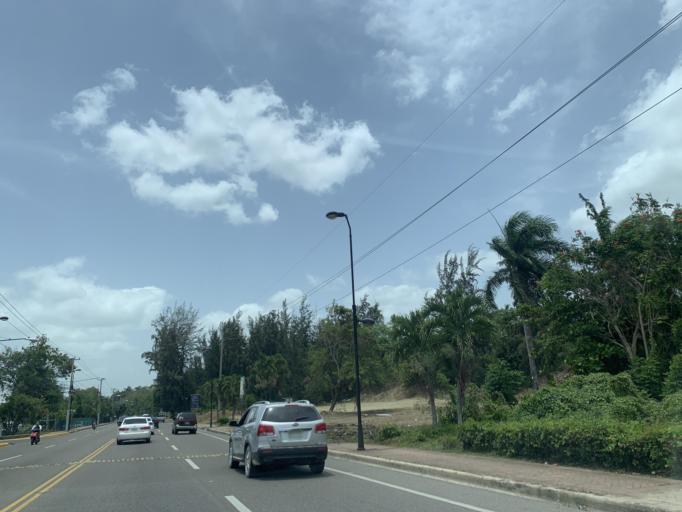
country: DO
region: Puerto Plata
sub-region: Puerto Plata
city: Puerto Plata
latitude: 19.7756
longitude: -70.6593
